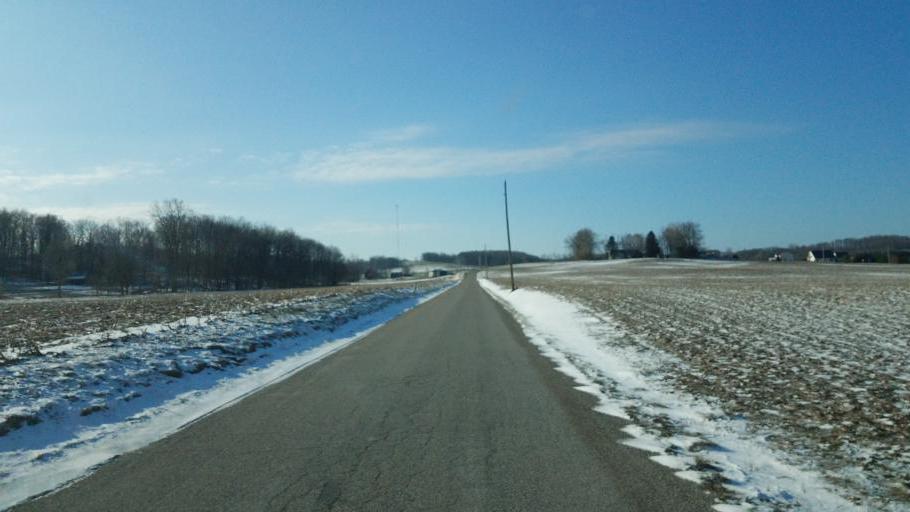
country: US
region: Ohio
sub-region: Sandusky County
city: Bellville
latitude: 40.6125
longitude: -82.5636
